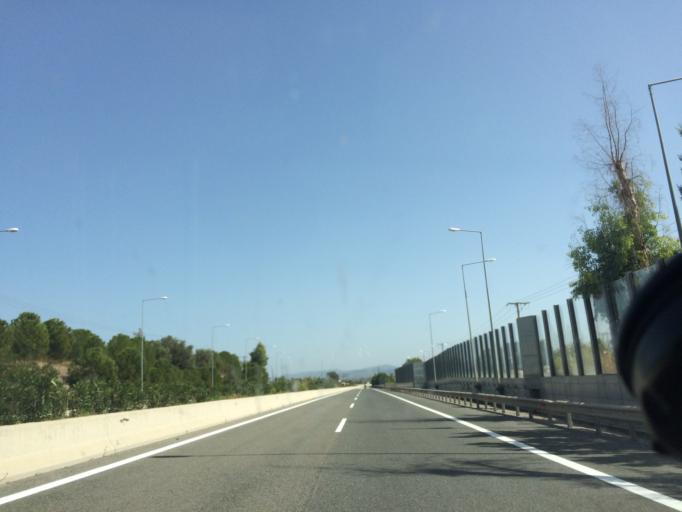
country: GR
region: Central Greece
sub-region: Nomos Voiotias
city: Schimatari
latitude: 38.3526
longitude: 23.5774
